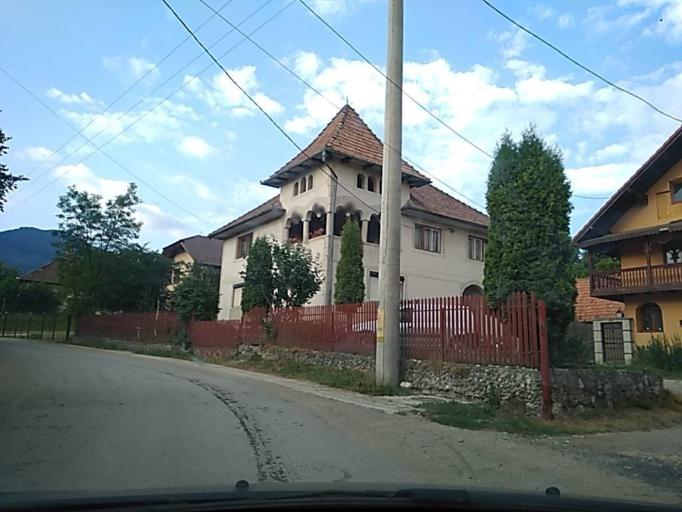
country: RO
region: Brasov
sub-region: Comuna Bran
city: Simon
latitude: 45.4998
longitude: 25.3837
